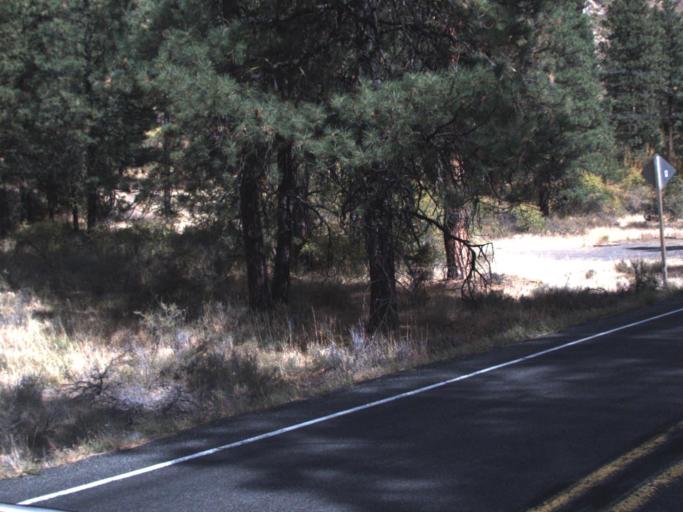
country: US
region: Washington
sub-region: Yakima County
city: Tieton
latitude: 46.6723
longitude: -121.0138
